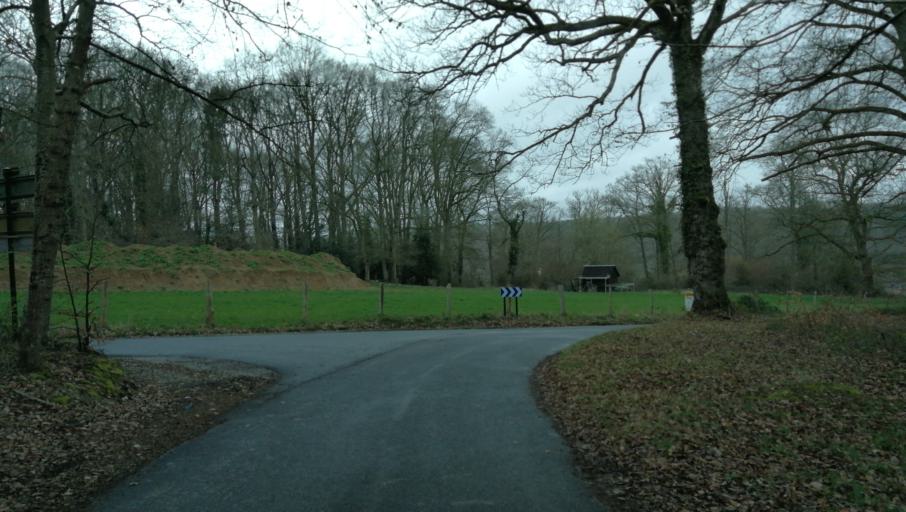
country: FR
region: Haute-Normandie
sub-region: Departement de l'Eure
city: Brionne
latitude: 49.1896
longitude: 0.7021
